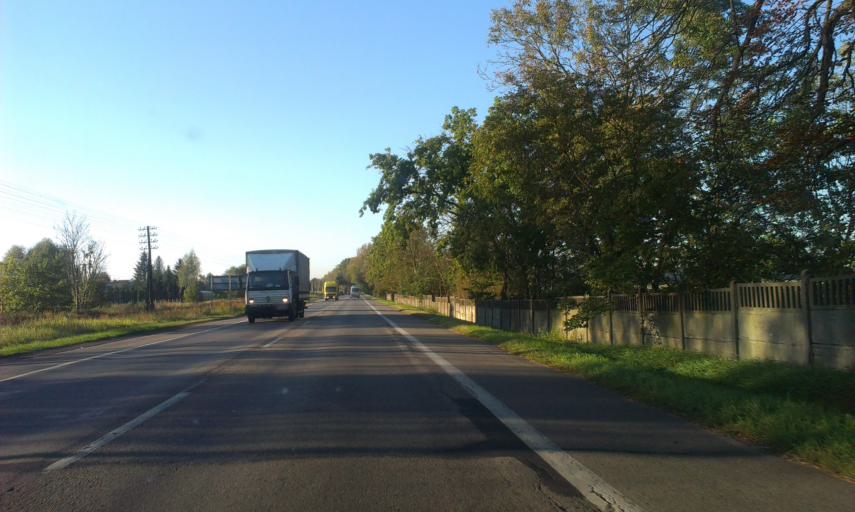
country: PL
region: Kujawsko-Pomorskie
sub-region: Powiat torunski
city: Lysomice
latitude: 53.0827
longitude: 18.6191
